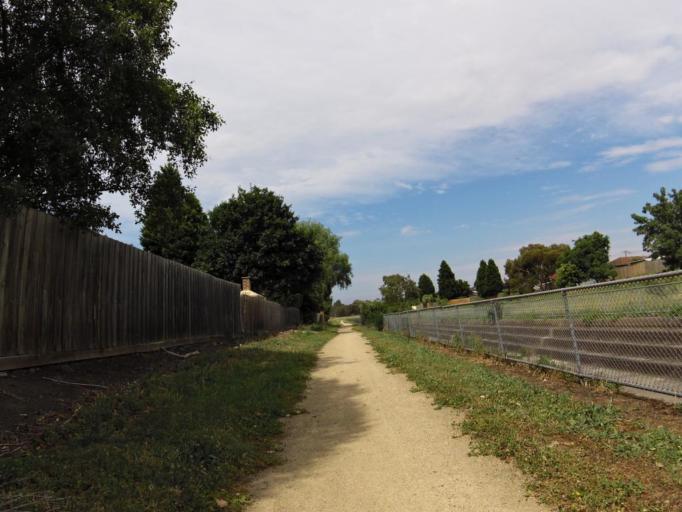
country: AU
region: Victoria
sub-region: Whittlesea
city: Epping
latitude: -37.6572
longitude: 145.0393
